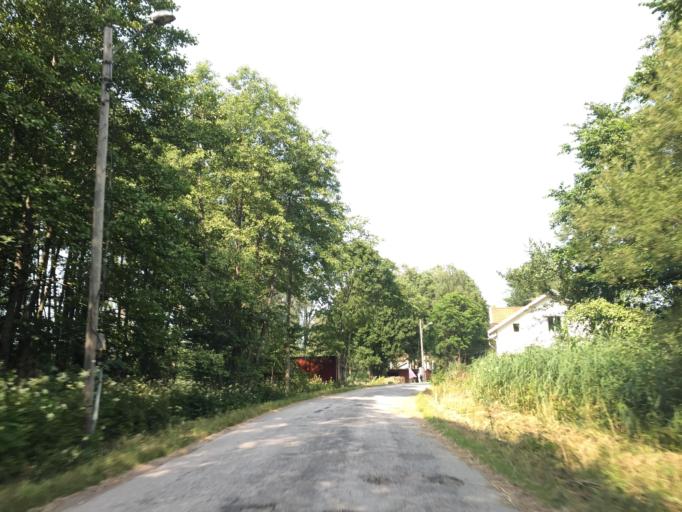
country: SE
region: Vaestra Goetaland
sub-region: Vanersborgs Kommun
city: Vanersborg
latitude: 58.3595
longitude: 12.2729
